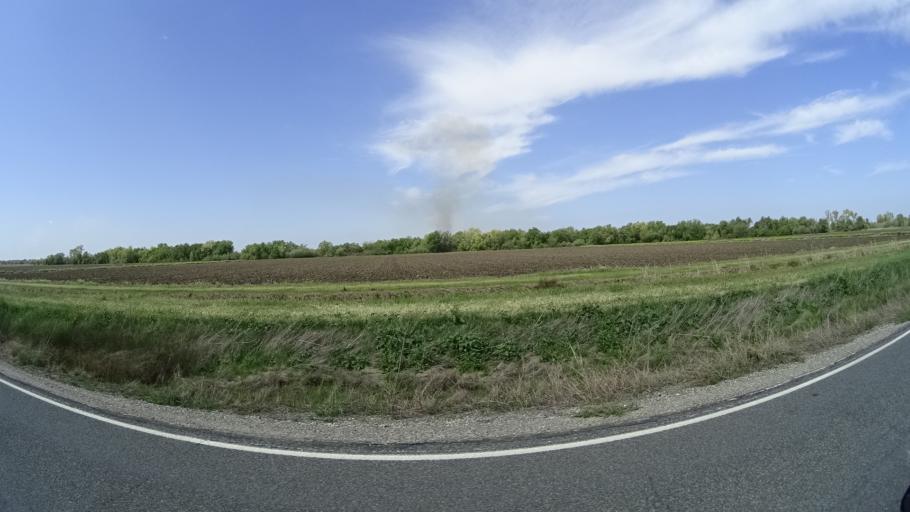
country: US
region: California
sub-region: Butte County
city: Durham
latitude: 39.5180
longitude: -121.8565
